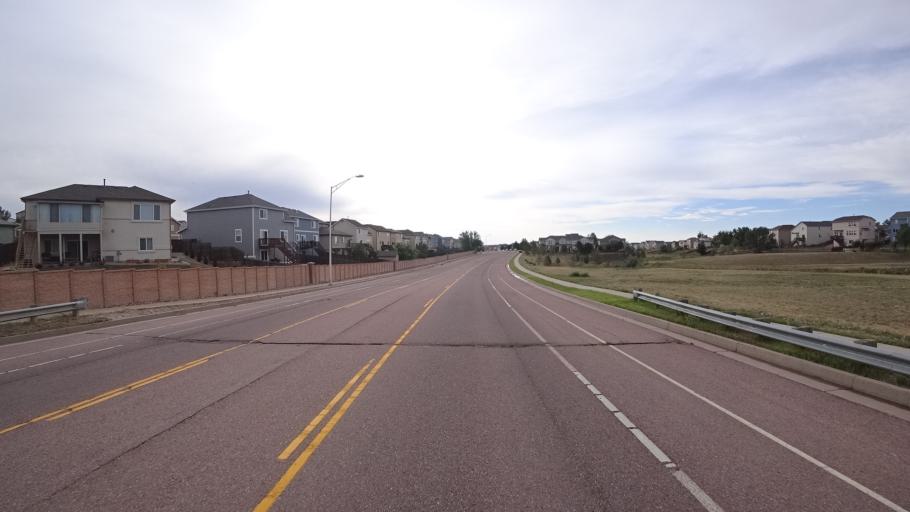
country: US
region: Colorado
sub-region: El Paso County
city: Fountain
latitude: 38.7155
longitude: -104.6946
